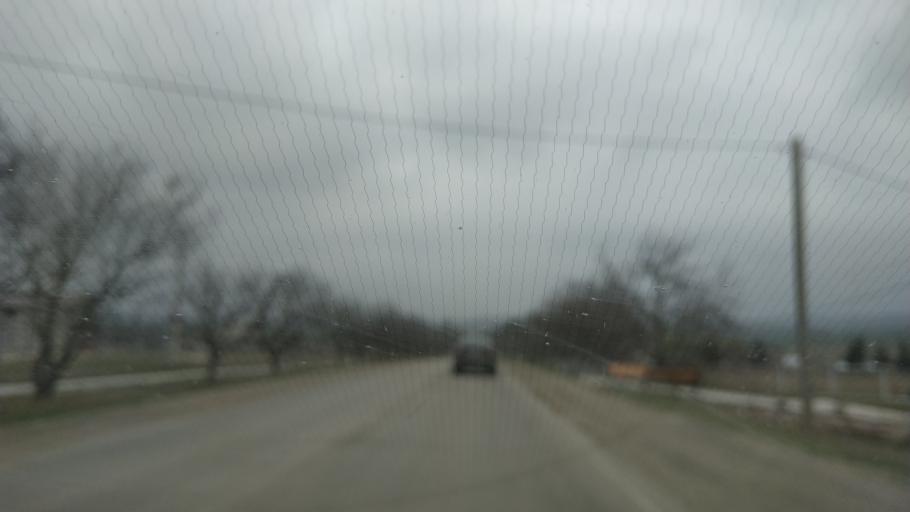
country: MD
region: Gagauzia
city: Comrat
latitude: 46.2843
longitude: 28.6765
